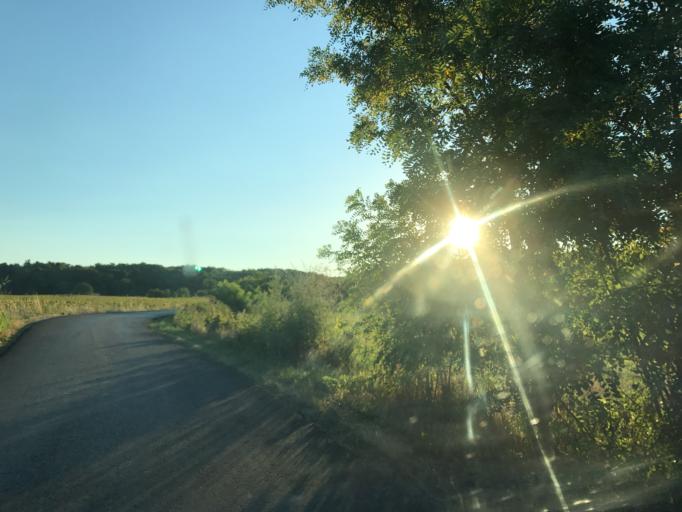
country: BG
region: Vidin
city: Bregovo
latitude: 44.1219
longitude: 22.5759
